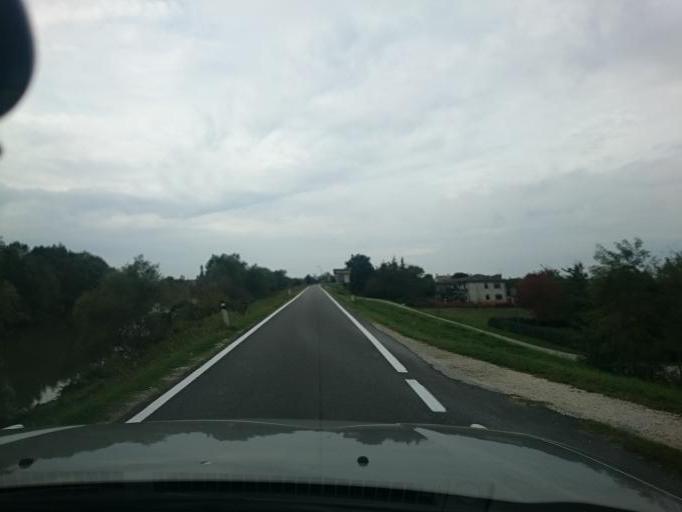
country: IT
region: Veneto
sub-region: Provincia di Padova
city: Correzzola
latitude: 45.2361
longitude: 12.0782
